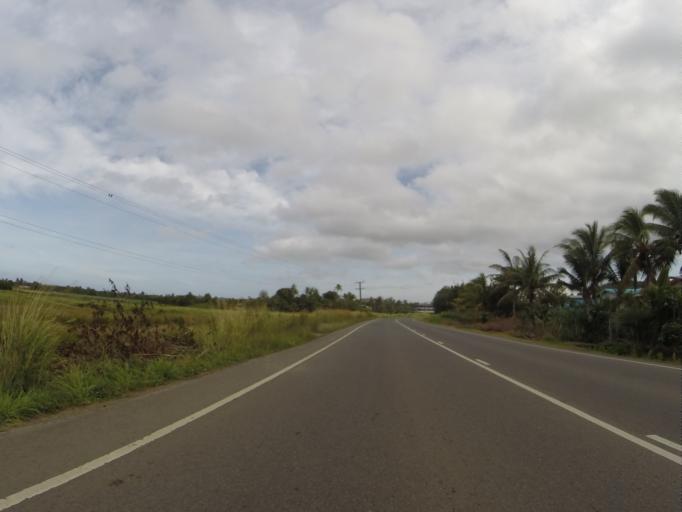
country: FJ
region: Western
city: Nadi
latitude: -18.1636
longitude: 177.5243
